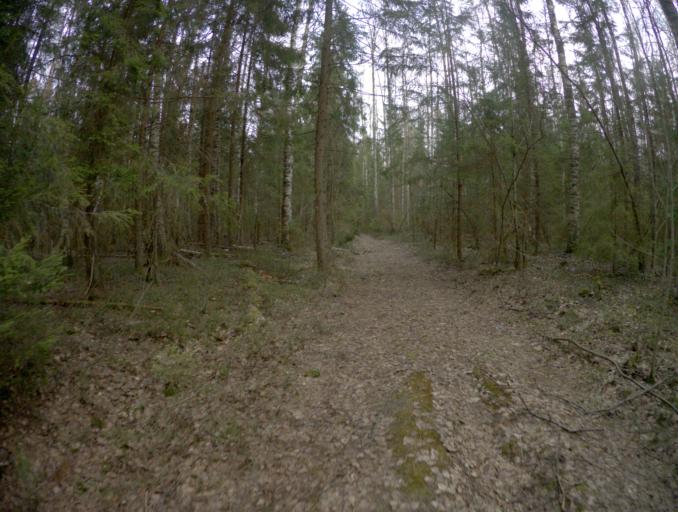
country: RU
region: Vladimir
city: Kommunar
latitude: 56.0788
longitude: 40.5247
